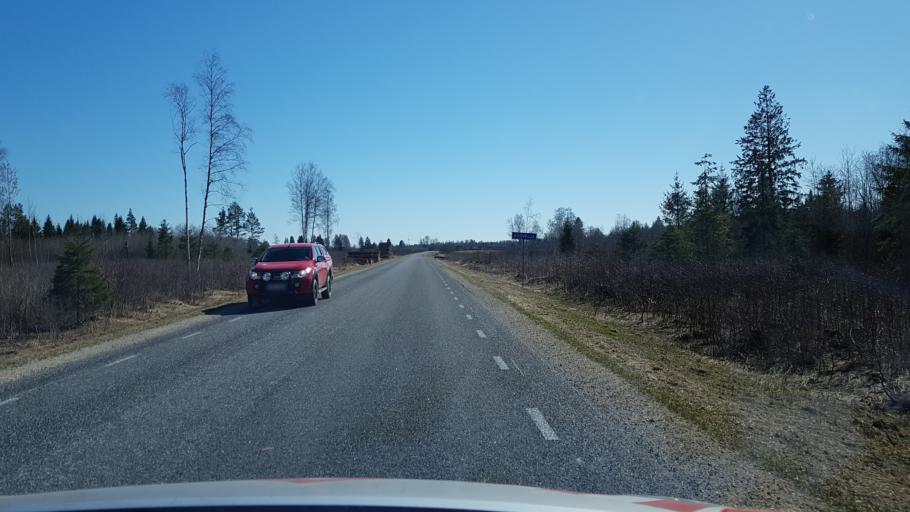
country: EE
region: Laeaene-Virumaa
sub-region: Someru vald
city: Someru
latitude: 59.3869
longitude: 26.4412
